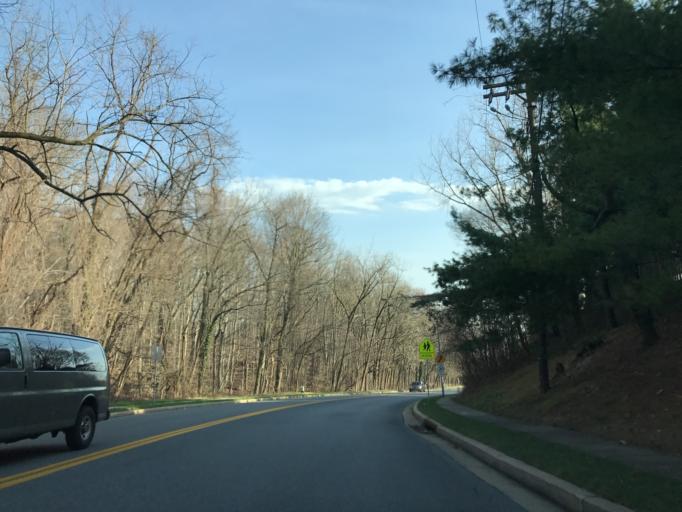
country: US
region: Maryland
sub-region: Baltimore County
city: Lutherville
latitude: 39.3755
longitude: -76.6607
